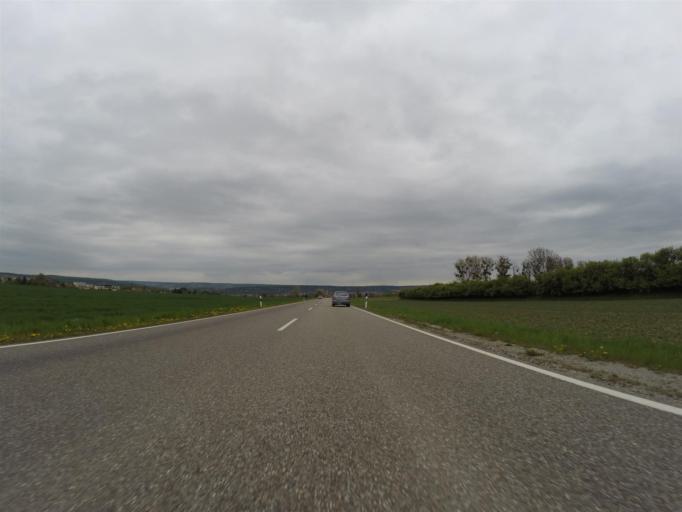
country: DE
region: Saxony-Anhalt
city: Naumburg
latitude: 51.1378
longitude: 11.7940
